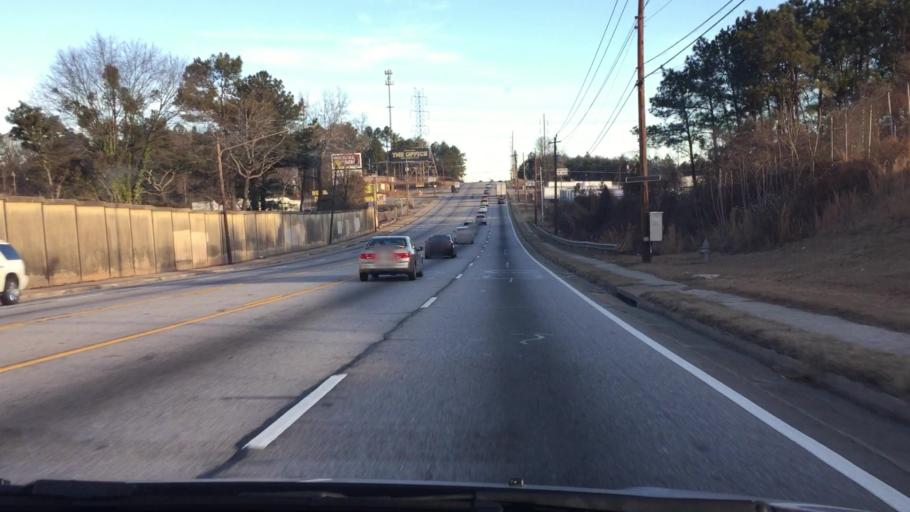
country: US
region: Georgia
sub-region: DeKalb County
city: Gresham Park
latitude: 33.7066
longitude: -84.3494
